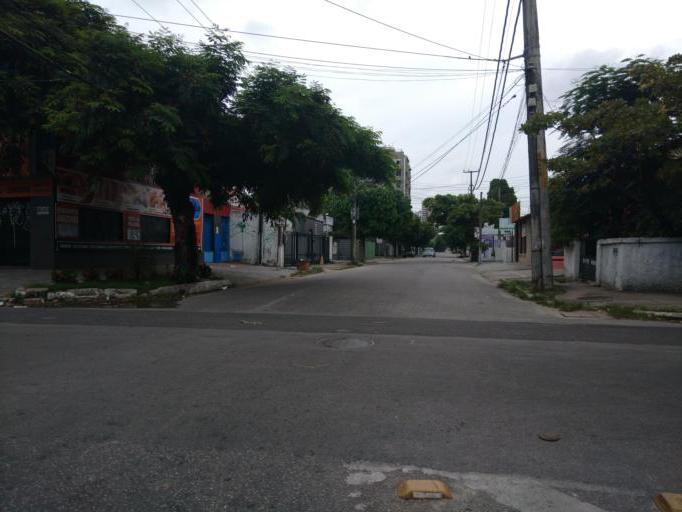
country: BR
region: Ceara
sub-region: Fortaleza
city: Fortaleza
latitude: -3.7359
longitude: -38.5059
